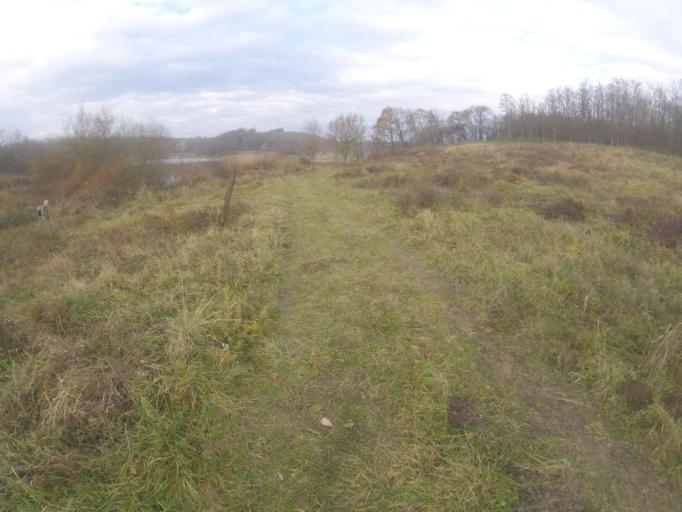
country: HU
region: Tolna
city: Bonyhad
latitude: 46.2635
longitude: 18.6220
